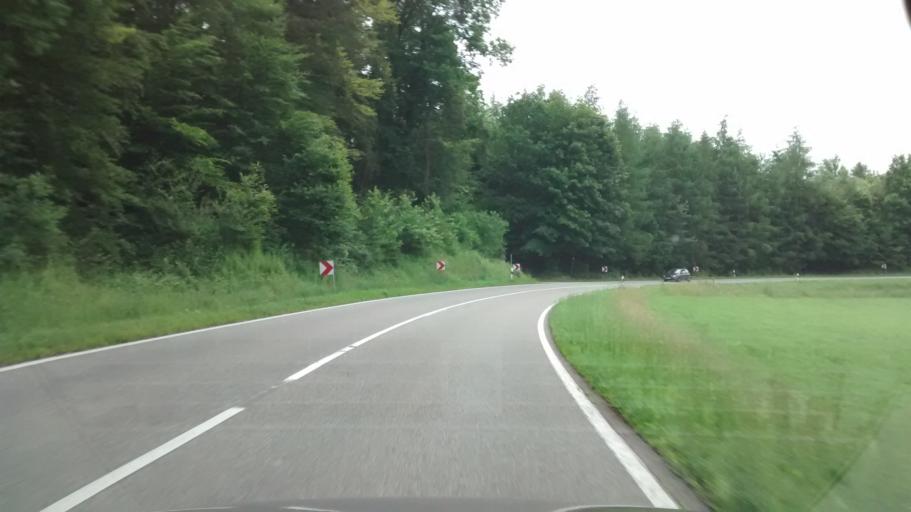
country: DE
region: Rheinland-Pfalz
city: Vorderweidenthal
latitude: 49.1212
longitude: 7.8582
